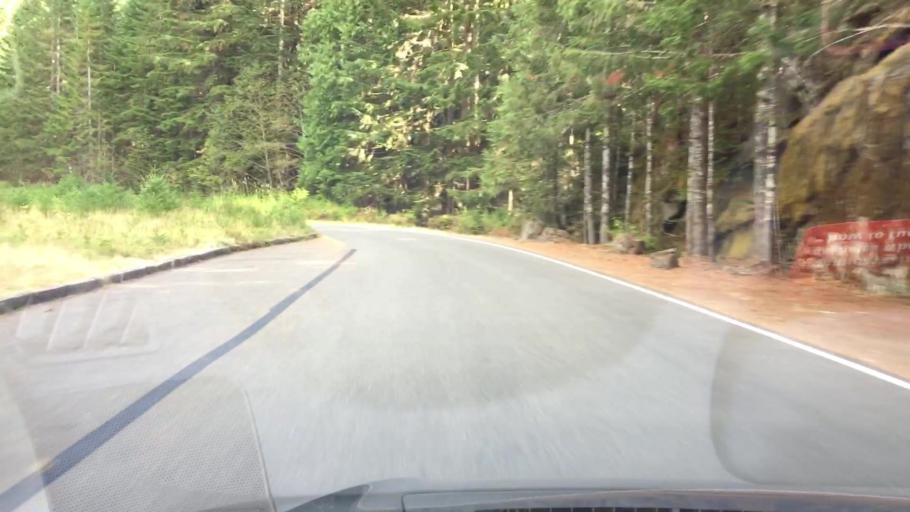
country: US
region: Washington
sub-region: Pierce County
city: Buckley
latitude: 46.7555
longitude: -121.5584
